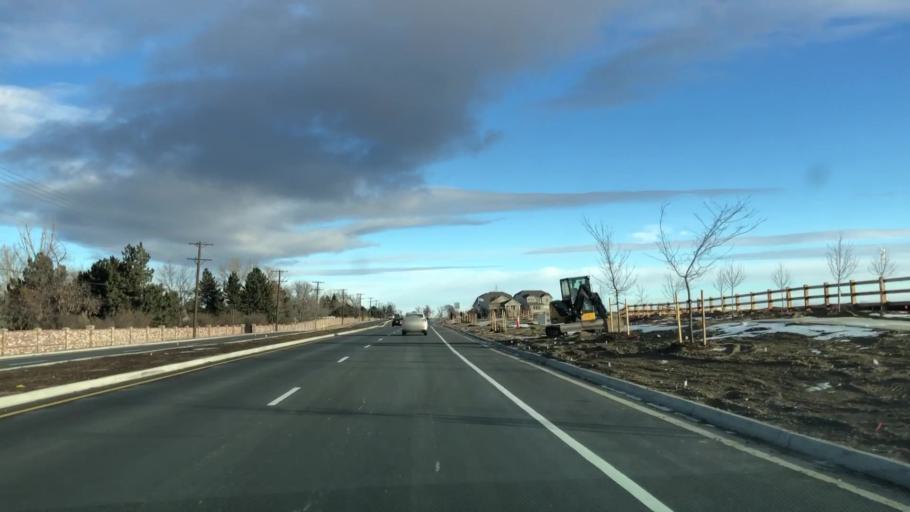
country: US
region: Colorado
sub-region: Larimer County
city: Loveland
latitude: 40.4213
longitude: -105.0208
